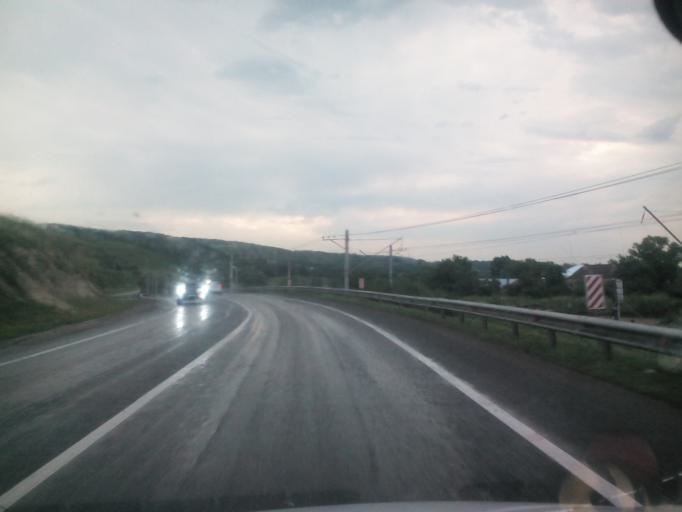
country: RU
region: Stavropol'skiy
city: Yasnaya Polyana
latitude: 44.0021
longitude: 42.7958
